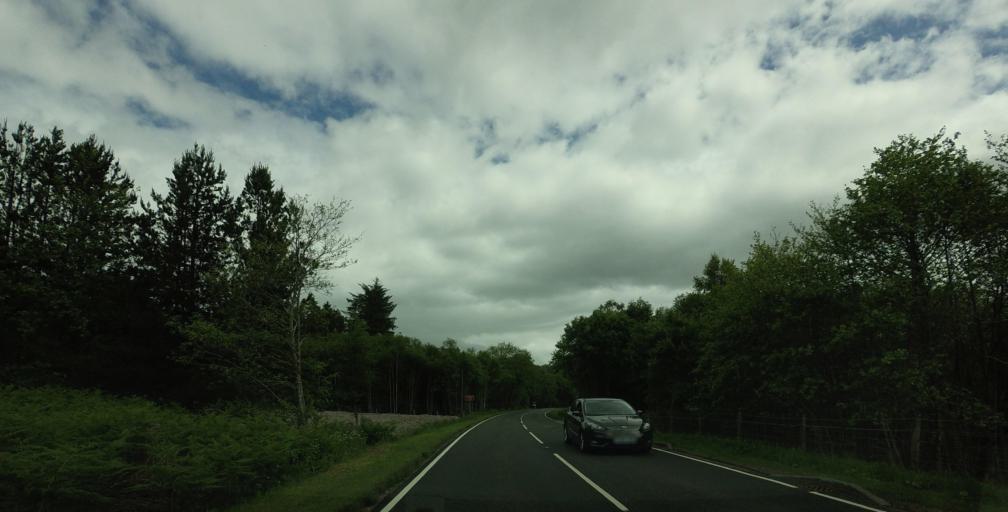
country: GB
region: Scotland
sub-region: Highland
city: Spean Bridge
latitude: 56.8953
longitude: -4.9057
